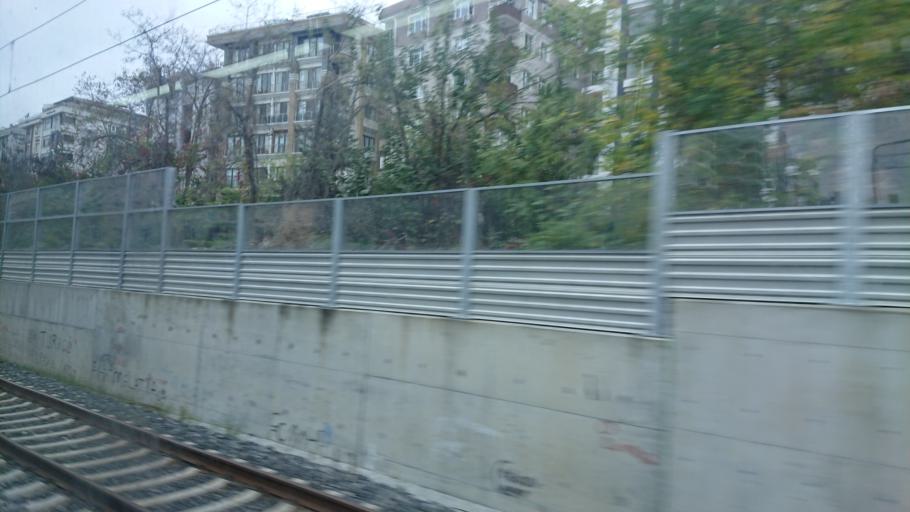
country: TR
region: Istanbul
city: Mahmutbey
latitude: 40.9926
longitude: 28.7706
